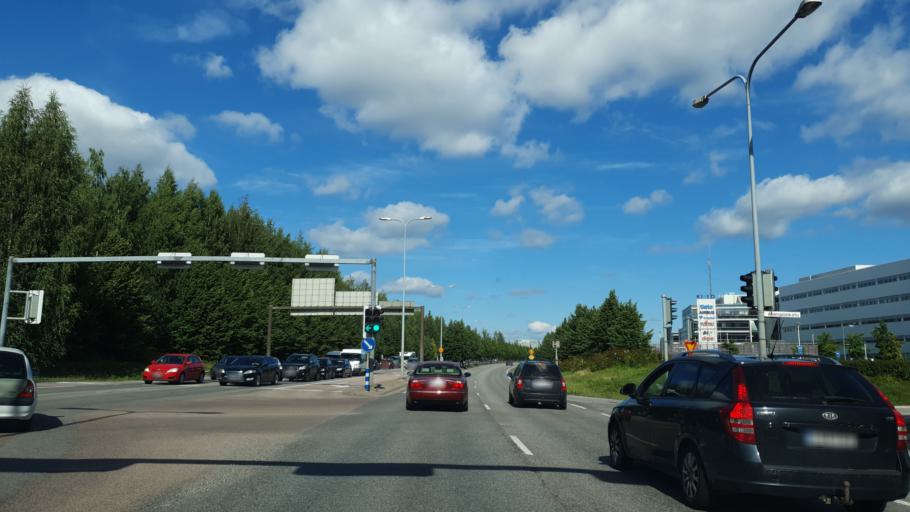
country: FI
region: Central Finland
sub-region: Jyvaeskylae
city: Jyvaeskylae
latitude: 62.2323
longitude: 25.7344
